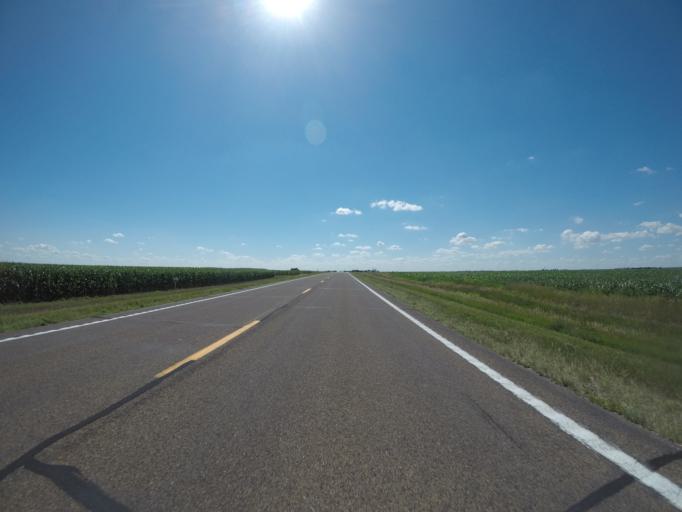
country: US
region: Nebraska
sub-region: Chase County
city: Imperial
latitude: 40.5372
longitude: -101.9549
